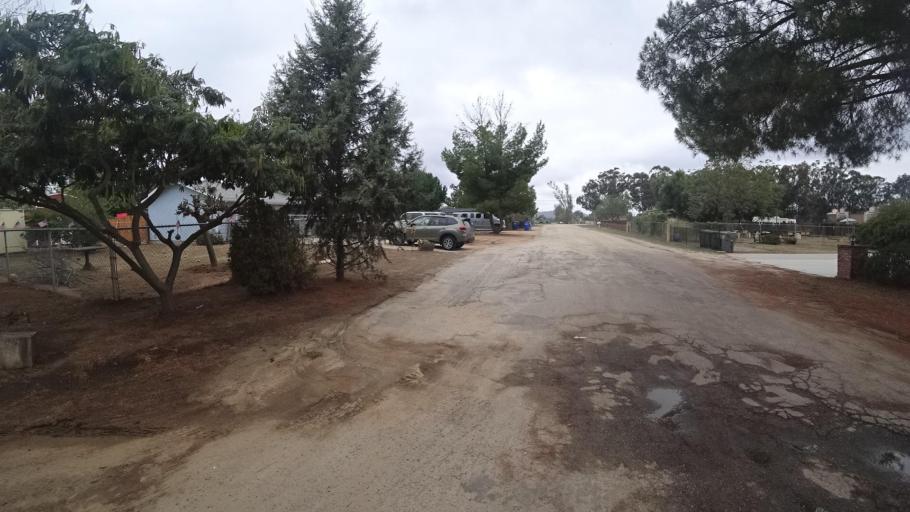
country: US
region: California
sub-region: San Diego County
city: Ramona
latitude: 33.0299
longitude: -116.8843
